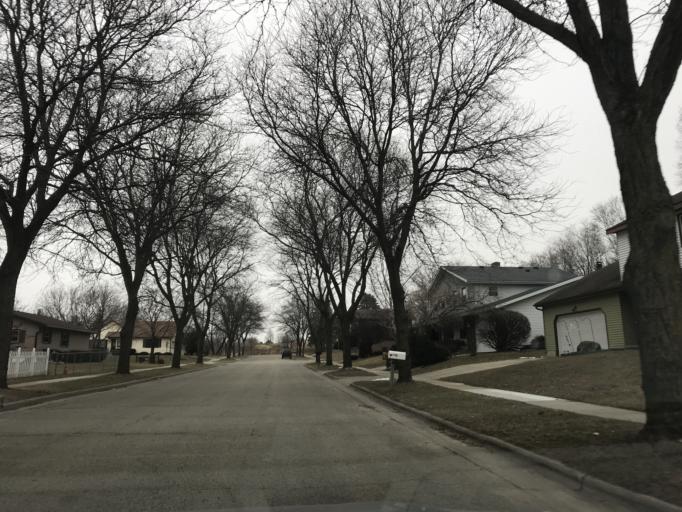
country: US
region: Wisconsin
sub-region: Dane County
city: Monona
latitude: 43.1009
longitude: -89.2929
